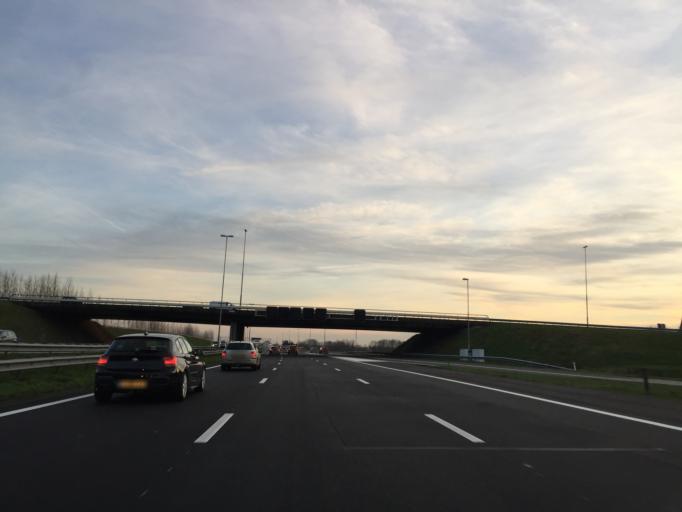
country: NL
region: North Brabant
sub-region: Gemeente Breda
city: Breda
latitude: 51.6464
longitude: 4.6913
